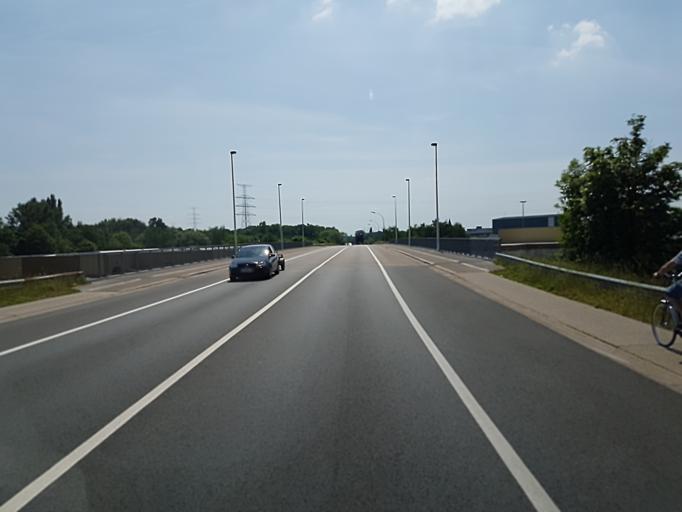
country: BE
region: Flanders
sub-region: Provincie Antwerpen
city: Dessel
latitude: 51.2261
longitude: 5.1153
